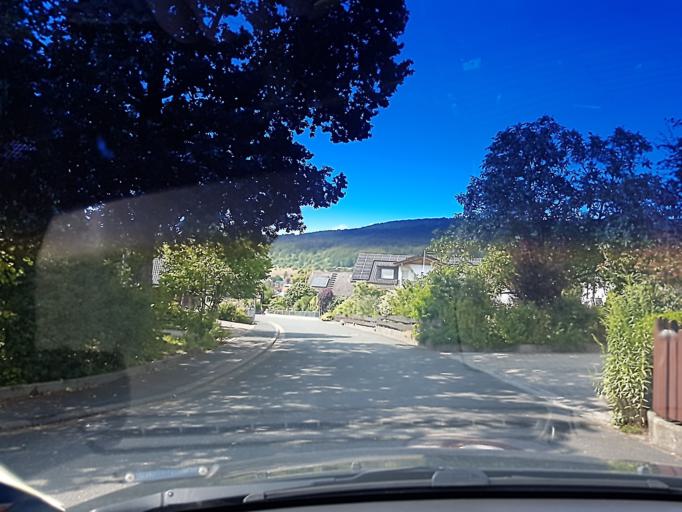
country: DE
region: Bavaria
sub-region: Upper Franconia
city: Litzendorf
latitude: 49.8712
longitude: 11.0489
